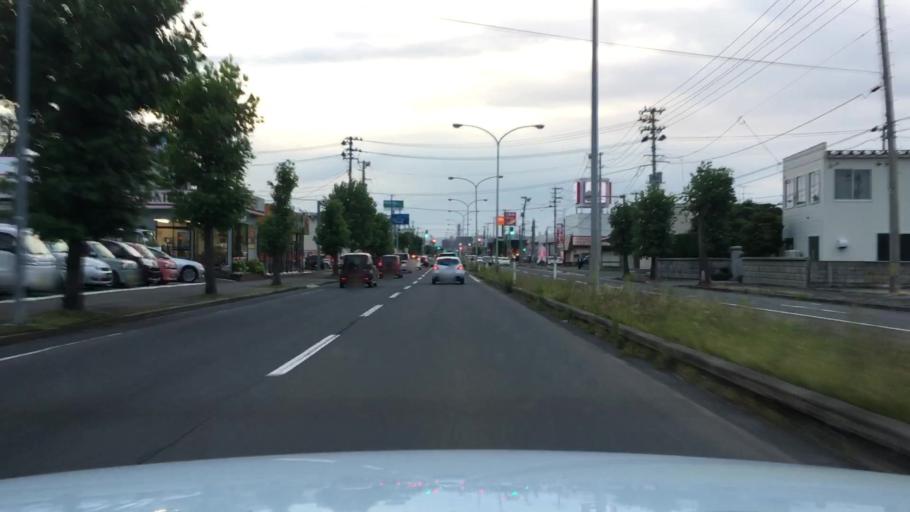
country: JP
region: Aomori
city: Hirosaki
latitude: 40.5963
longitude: 140.5013
